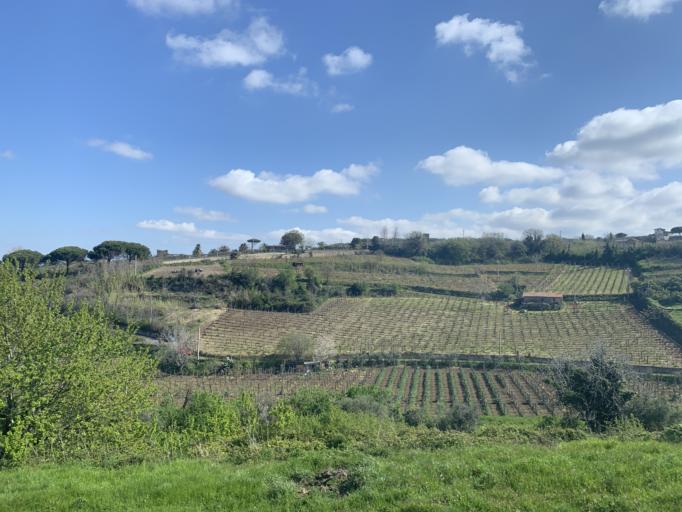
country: IT
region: Latium
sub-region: Citta metropolitana di Roma Capitale
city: Grottaferrata
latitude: 41.7836
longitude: 12.6512
